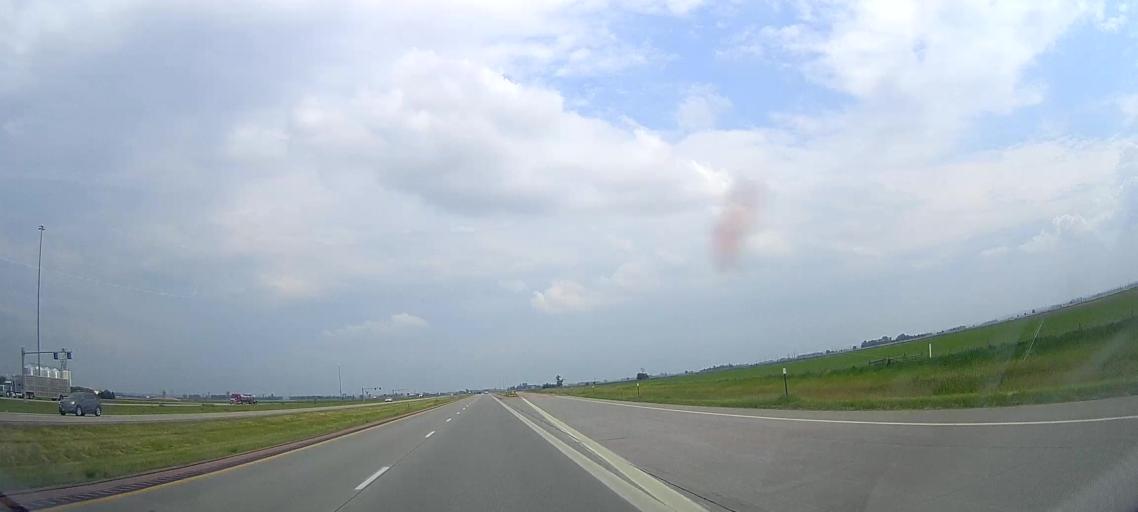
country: US
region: South Dakota
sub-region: Union County
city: Elk Point
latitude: 42.6459
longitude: -96.6311
